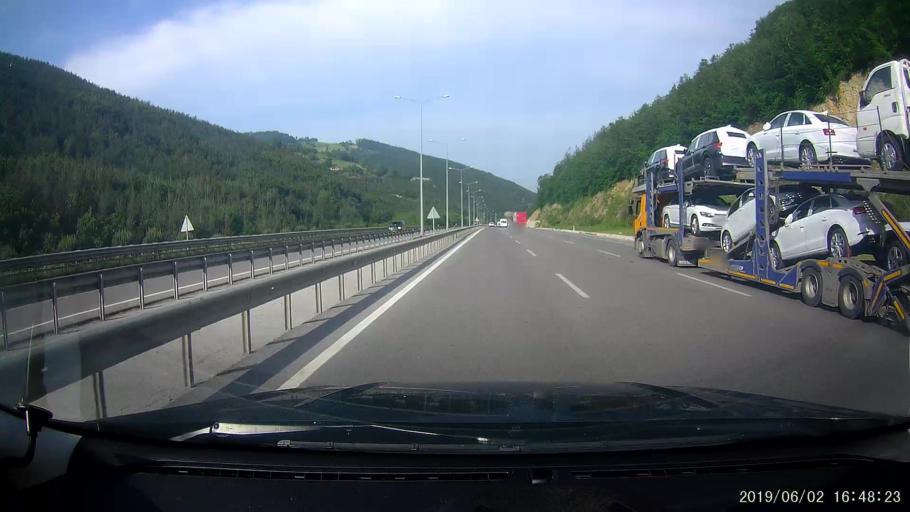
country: TR
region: Samsun
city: Kavak
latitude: 41.2267
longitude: 36.1347
